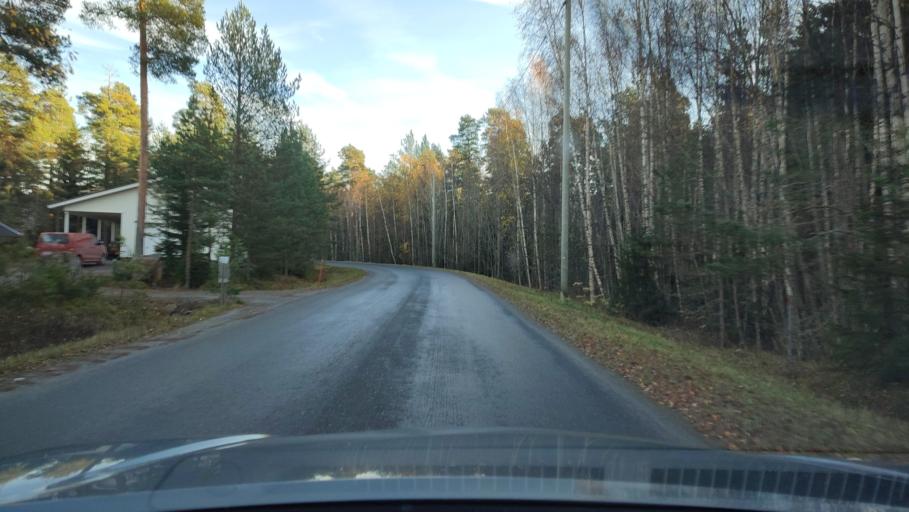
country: FI
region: Ostrobothnia
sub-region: Vaasa
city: Teeriniemi
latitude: 63.0670
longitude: 21.6918
